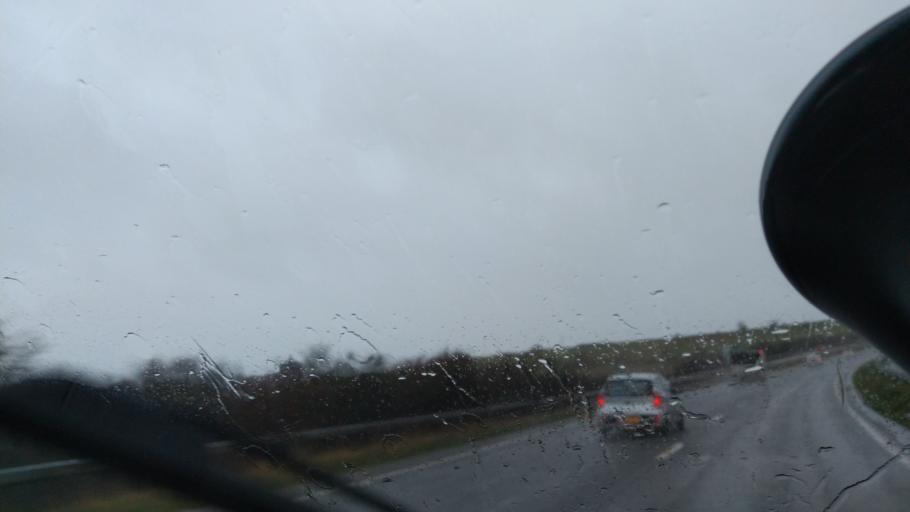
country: GB
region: England
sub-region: East Sussex
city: Portslade
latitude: 50.8532
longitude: -0.2118
